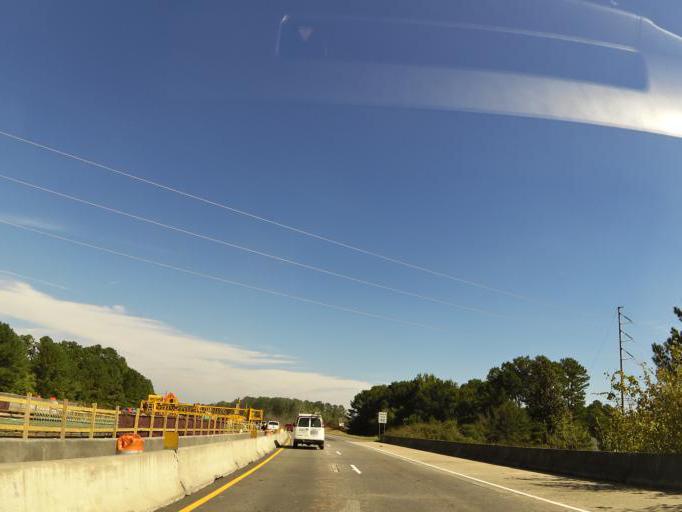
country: US
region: Georgia
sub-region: Cherokee County
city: Woodstock
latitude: 34.0571
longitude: -84.5434
